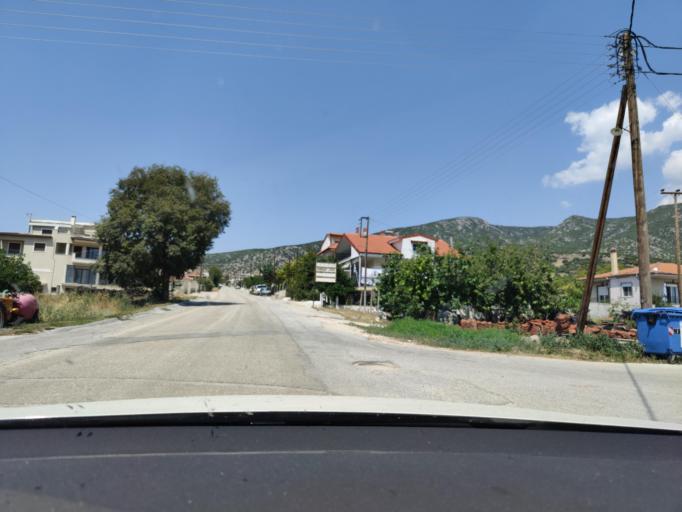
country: GR
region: East Macedonia and Thrace
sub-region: Nomos Kavalas
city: Paralia Ofryniou
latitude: 40.7978
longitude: 23.9537
